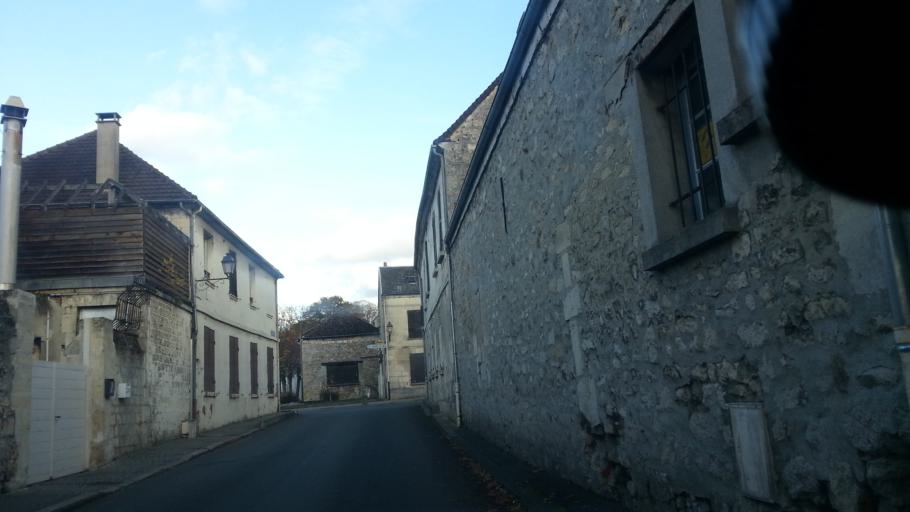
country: FR
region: Picardie
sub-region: Departement de l'Oise
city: Fleurines
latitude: 49.2588
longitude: 2.5837
